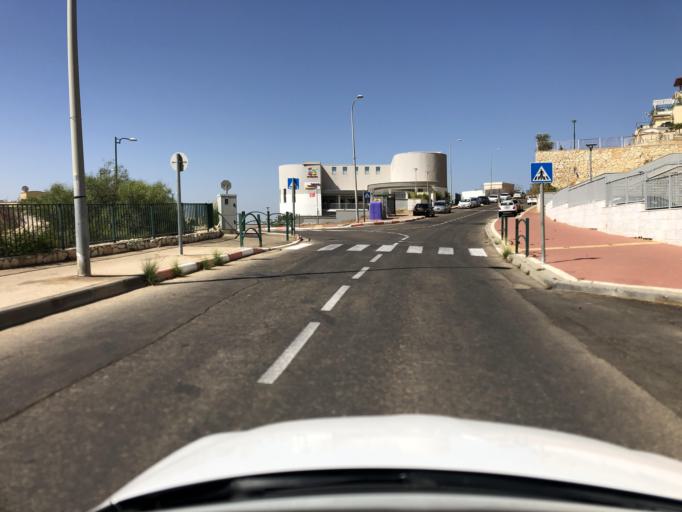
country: PS
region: West Bank
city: An Nabi Ilyas
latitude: 32.1656
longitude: 35.0200
